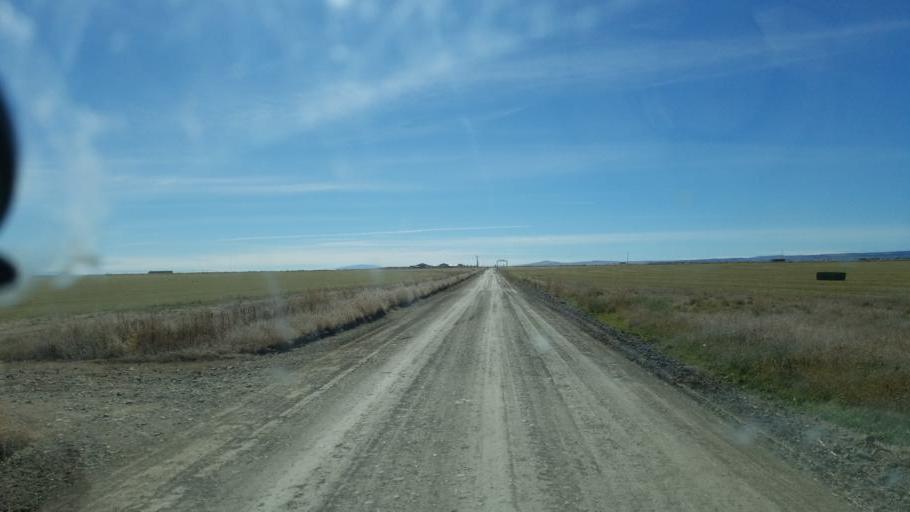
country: US
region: Colorado
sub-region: Rio Grande County
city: Monte Vista
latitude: 37.4063
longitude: -106.1305
